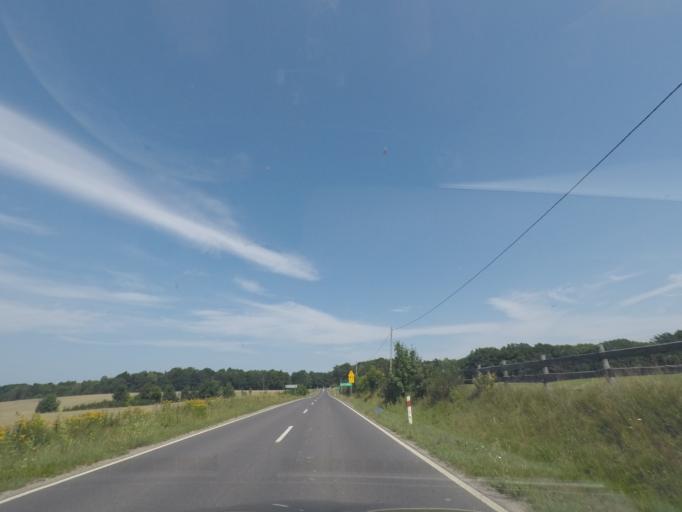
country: PL
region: West Pomeranian Voivodeship
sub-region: Powiat koszalinski
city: Sianow
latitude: 54.2681
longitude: 16.2678
